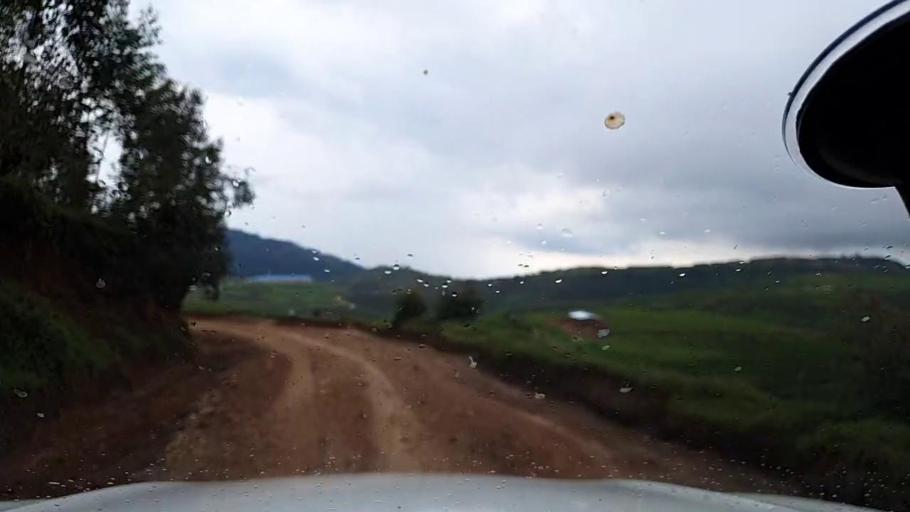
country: RW
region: Western Province
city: Kibuye
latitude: -2.0954
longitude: 29.4886
